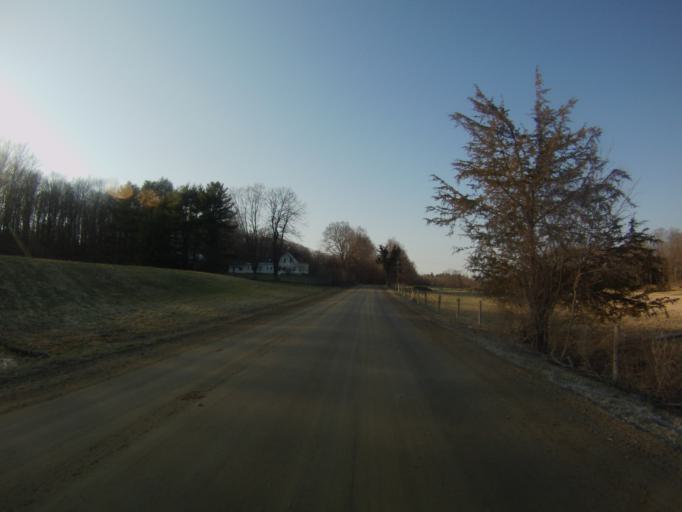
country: US
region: Vermont
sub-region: Addison County
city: Middlebury (village)
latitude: 44.0374
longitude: -73.1458
